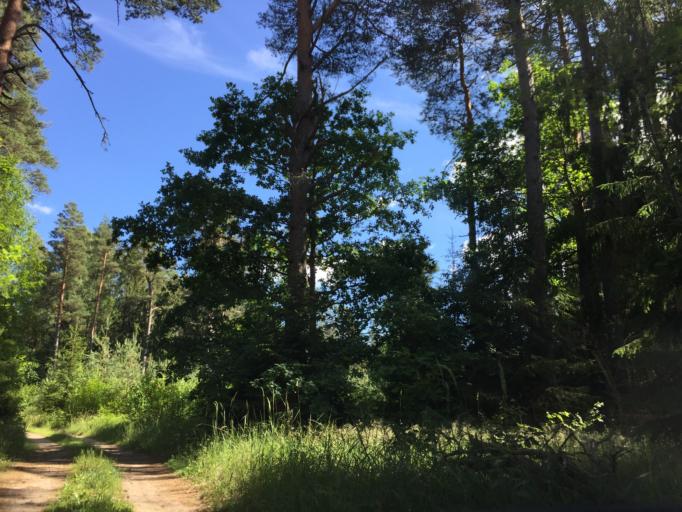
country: LV
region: Ventspils Rajons
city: Piltene
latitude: 57.1010
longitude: 21.8017
